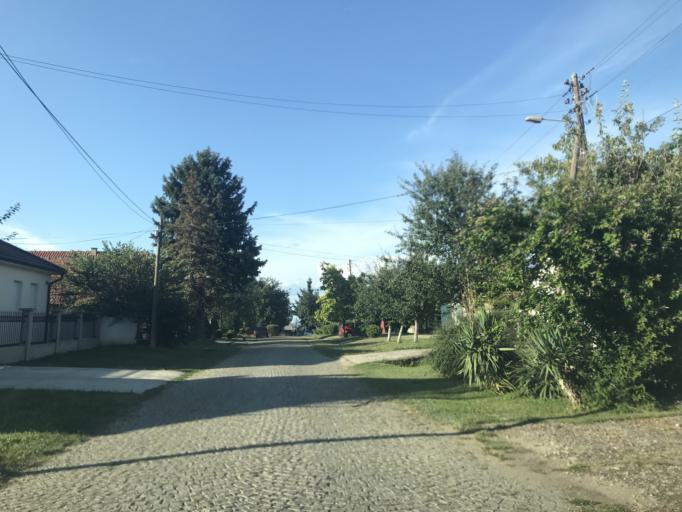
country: RS
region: Autonomna Pokrajina Vojvodina
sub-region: Juznobacki Okrug
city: Novi Sad
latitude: 45.2102
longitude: 19.8023
